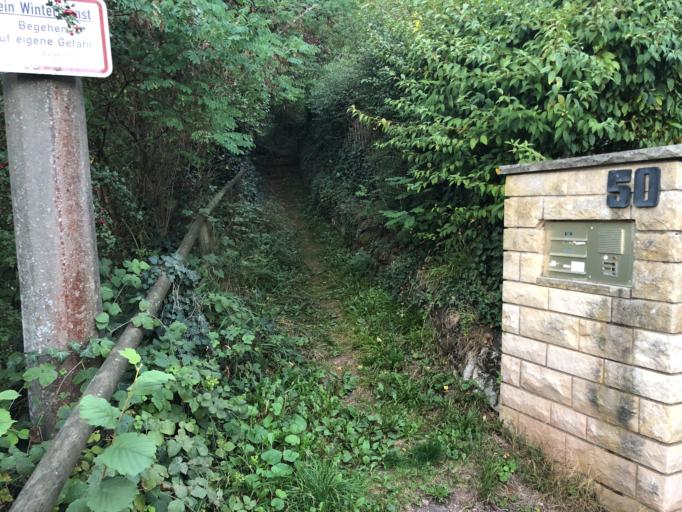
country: DE
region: Baden-Wuerttemberg
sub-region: Tuebingen Region
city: Tuebingen
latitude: 48.5143
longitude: 9.0380
